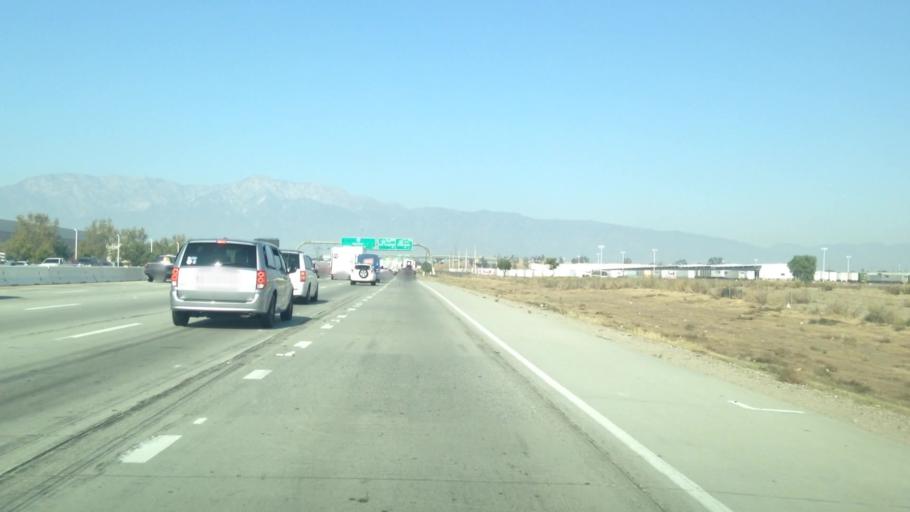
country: US
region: California
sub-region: Riverside County
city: Mira Loma
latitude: 34.0085
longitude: -117.5501
